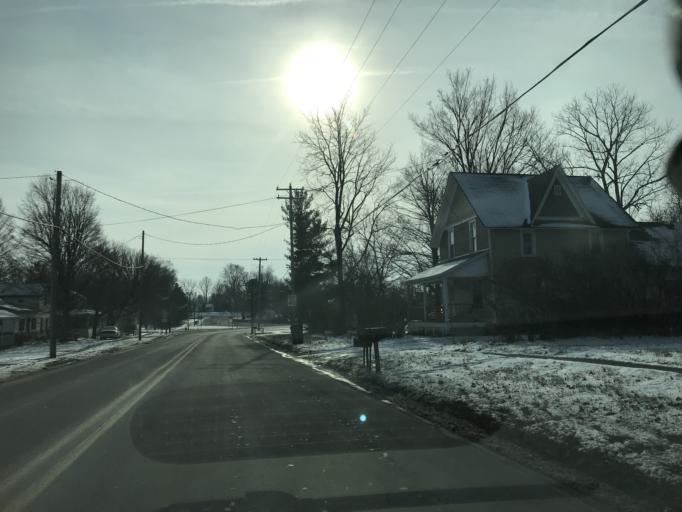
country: US
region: Michigan
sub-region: Barry County
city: Nashville
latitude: 42.5985
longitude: -85.0938
